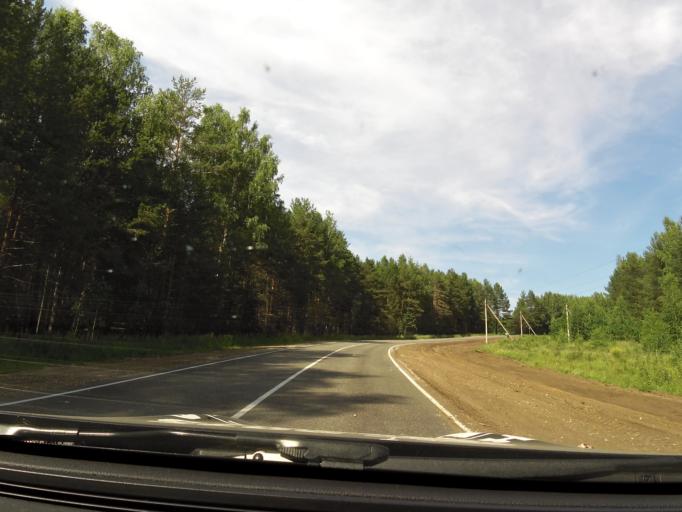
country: RU
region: Kirov
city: Belaya Kholunitsa
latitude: 58.8401
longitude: 50.6877
